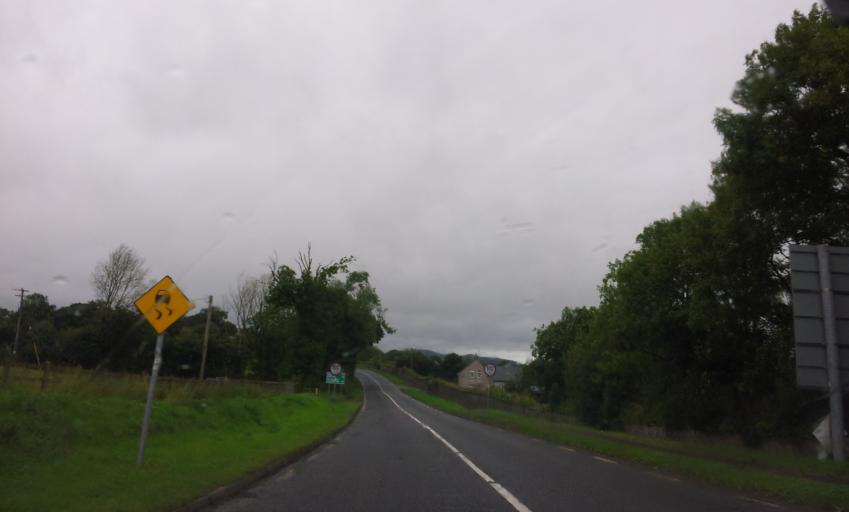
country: IE
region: Munster
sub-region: County Cork
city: Mitchelstown
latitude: 52.2651
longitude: -8.2916
